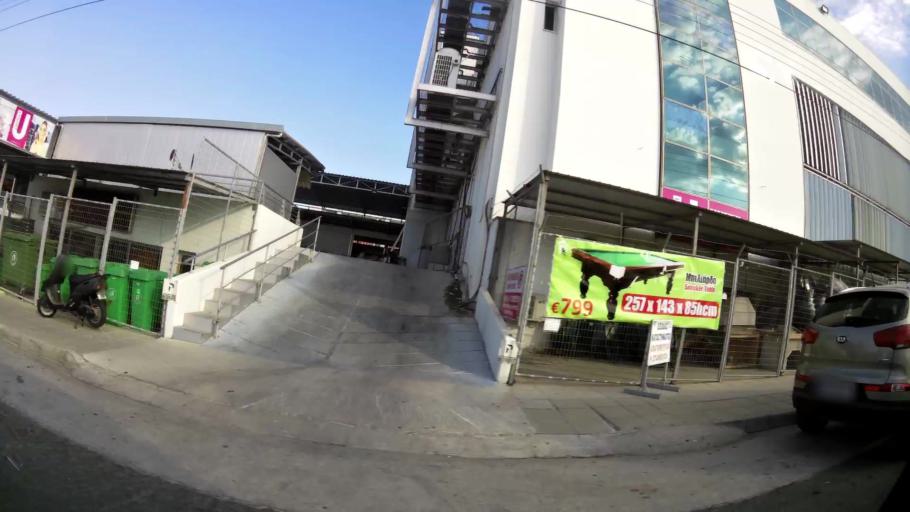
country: CY
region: Larnaka
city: Larnaca
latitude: 34.9292
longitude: 33.6037
